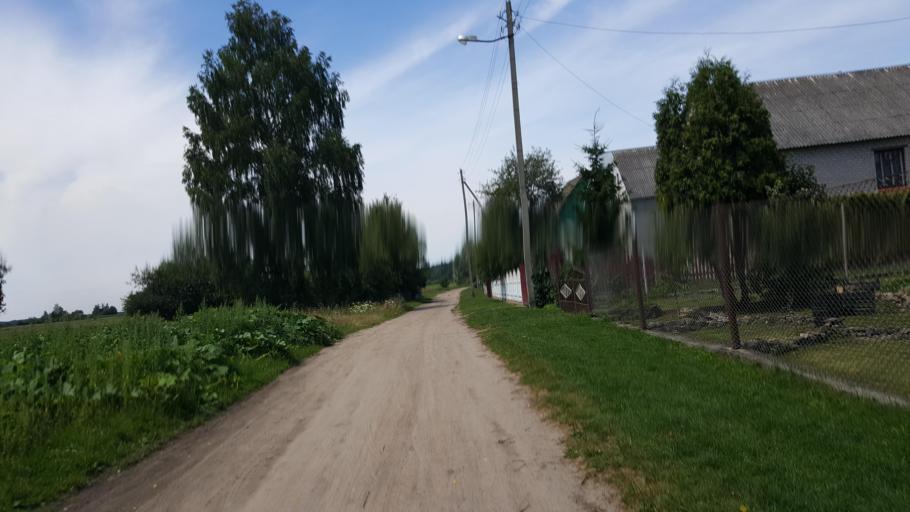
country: BY
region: Brest
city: Pruzhany
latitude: 52.5603
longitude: 24.2085
